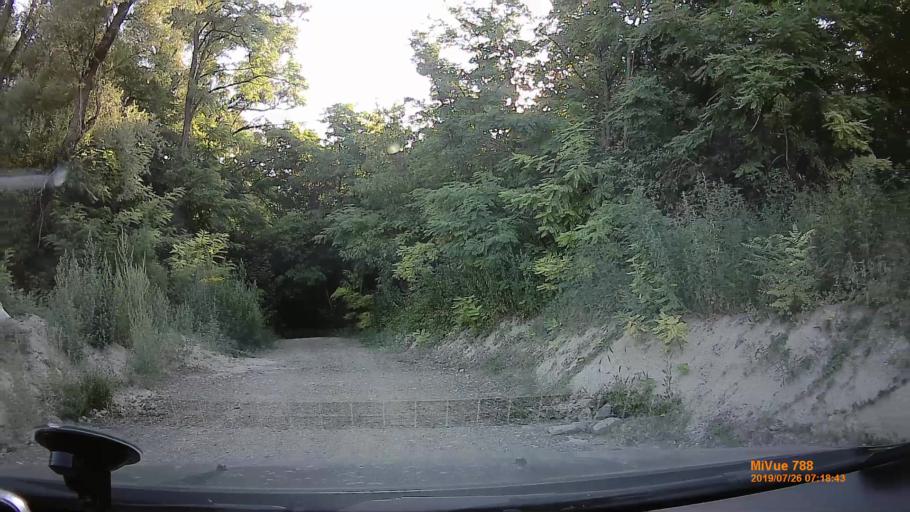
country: HU
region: Pest
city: Mogyorod
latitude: 47.5938
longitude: 19.2301
